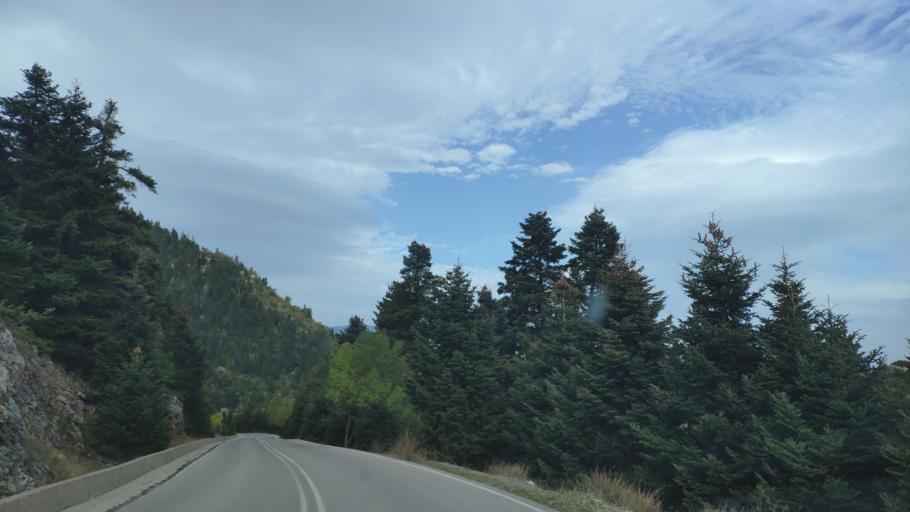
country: GR
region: Central Greece
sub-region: Nomos Fokidos
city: Amfissa
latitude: 38.6618
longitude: 22.3810
